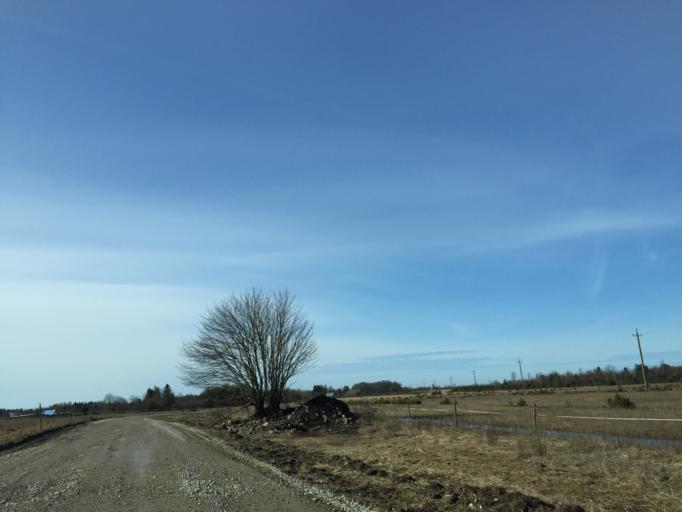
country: EE
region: Laeaene
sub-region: Haapsalu linn
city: Haapsalu
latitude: 58.6712
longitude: 23.5380
